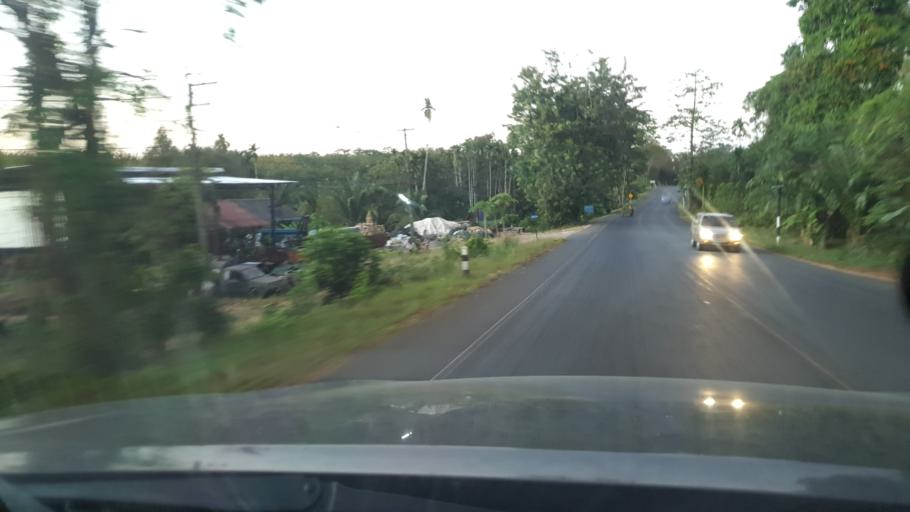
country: TH
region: Phangnga
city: Khura Buri
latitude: 9.1982
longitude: 98.3893
